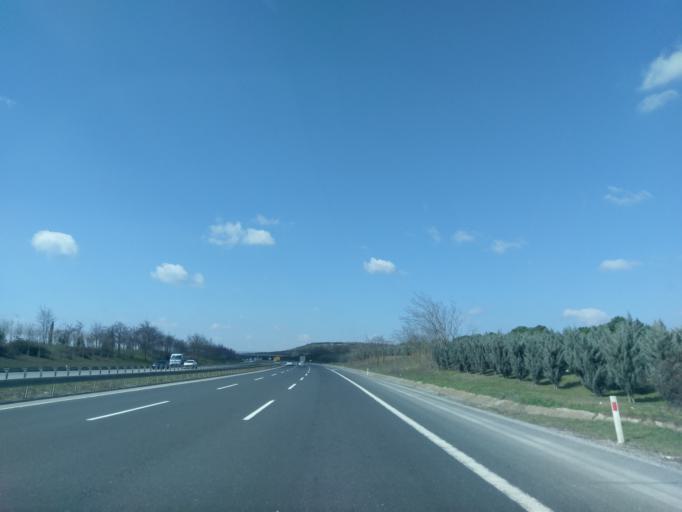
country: TR
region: Istanbul
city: Canta
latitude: 41.1562
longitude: 28.1414
